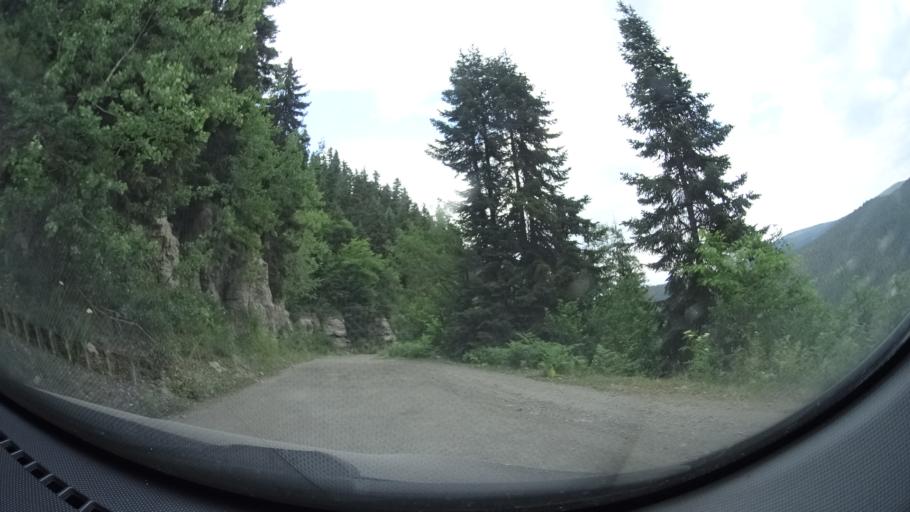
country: GE
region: Samtskhe-Javakheti
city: Adigeni
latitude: 41.6413
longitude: 42.5902
